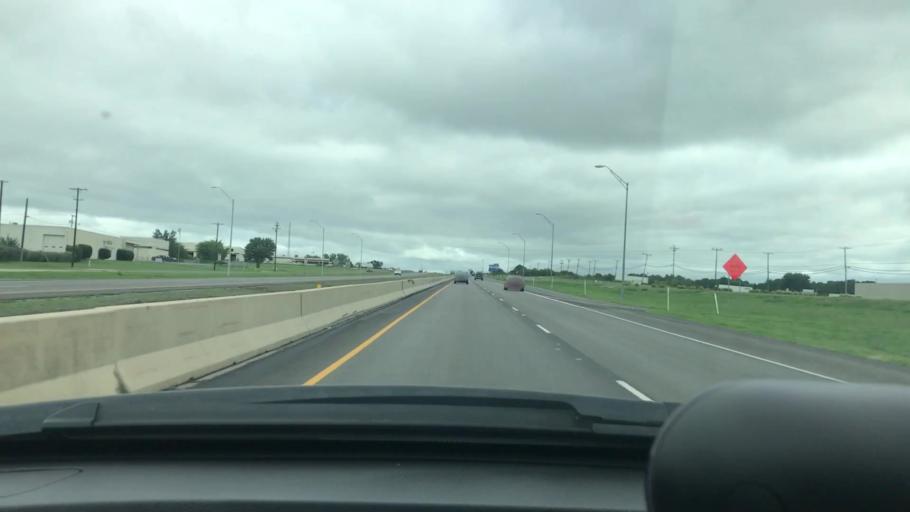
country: US
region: Texas
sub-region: Grayson County
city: Sherman
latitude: 33.5835
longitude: -96.6034
